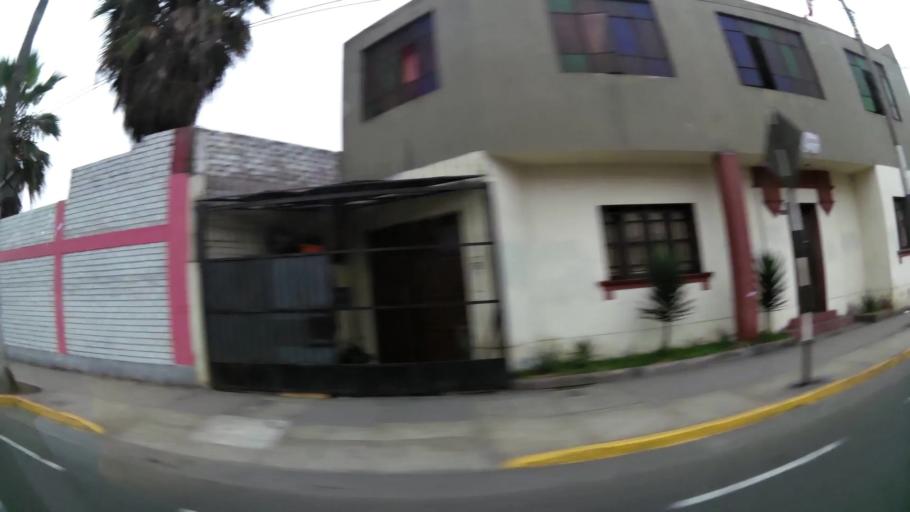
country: PE
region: Lima
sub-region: Lima
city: Surco
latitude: -12.1653
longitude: -77.0215
